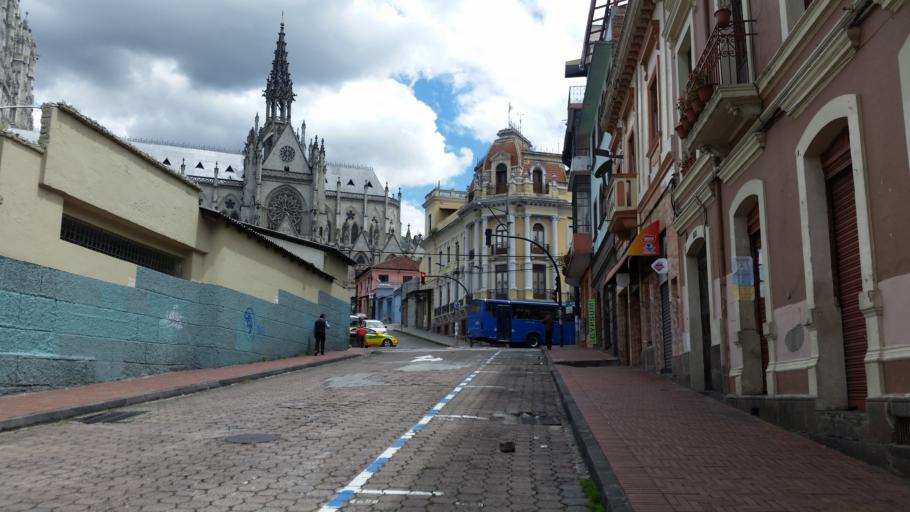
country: EC
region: Pichincha
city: Quito
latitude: -0.2158
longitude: -78.5060
